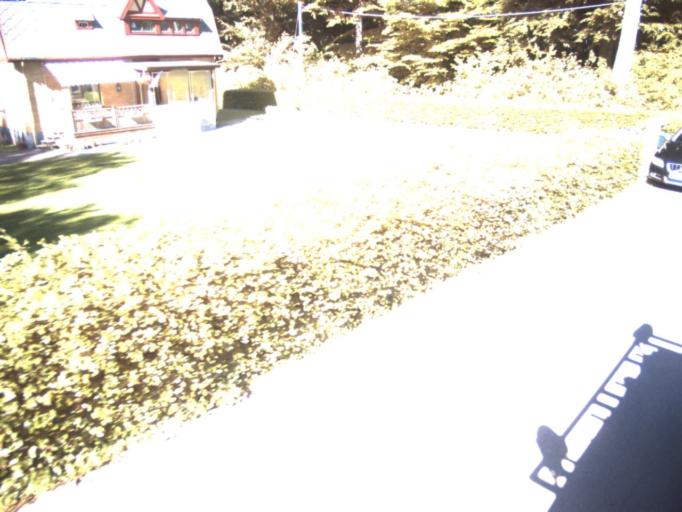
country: SE
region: Skane
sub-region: Helsingborg
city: Odakra
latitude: 56.0998
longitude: 12.7352
